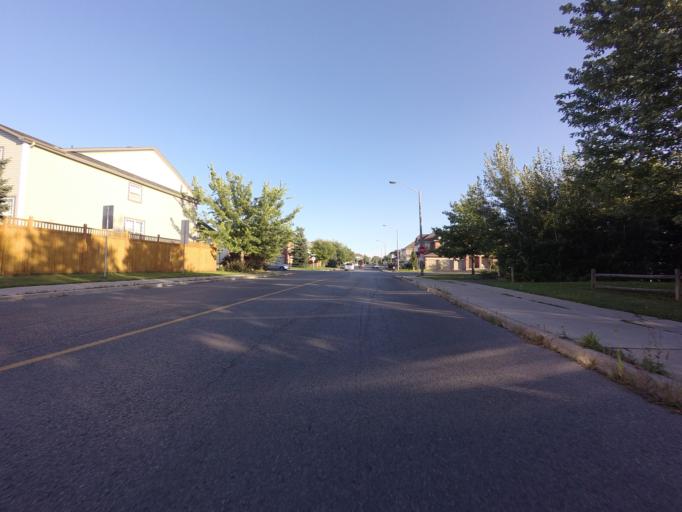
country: CA
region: Ontario
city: Bells Corners
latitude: 45.2804
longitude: -75.7374
